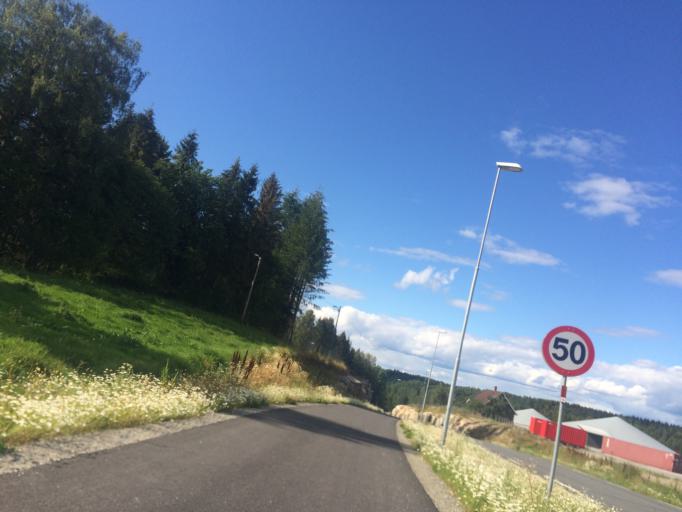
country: NO
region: Akershus
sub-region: As
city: As
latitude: 59.6754
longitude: 10.7620
